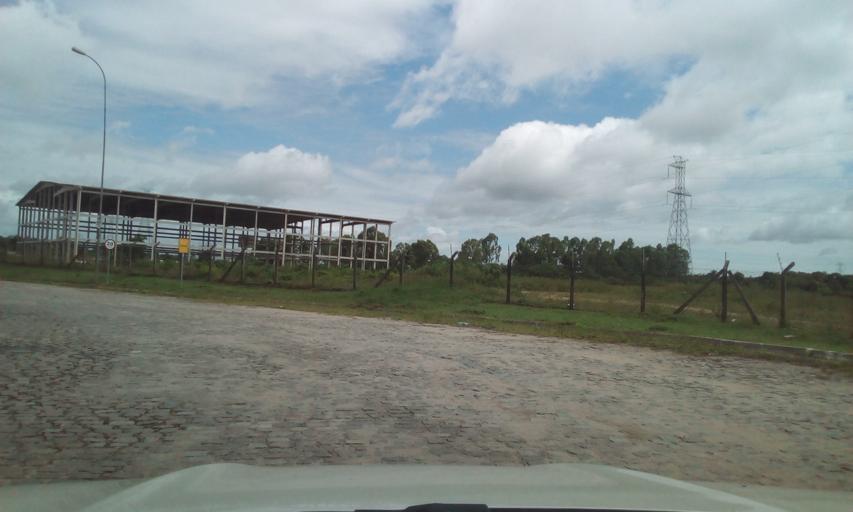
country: BR
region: Paraiba
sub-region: Conde
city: Conde
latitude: -7.1912
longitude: -34.8962
